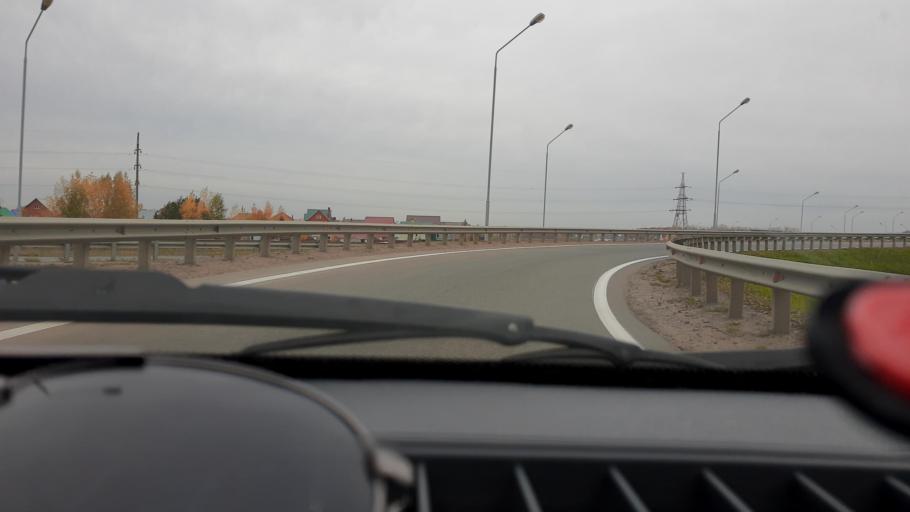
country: RU
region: Bashkortostan
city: Ufa
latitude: 54.6435
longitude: 55.9307
